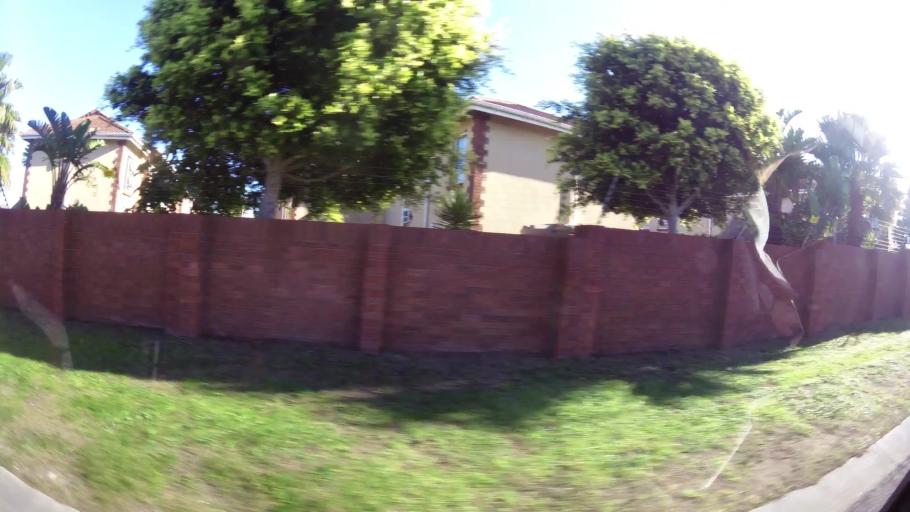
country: ZA
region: Eastern Cape
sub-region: Nelson Mandela Bay Metropolitan Municipality
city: Port Elizabeth
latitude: -33.9795
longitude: 25.6299
